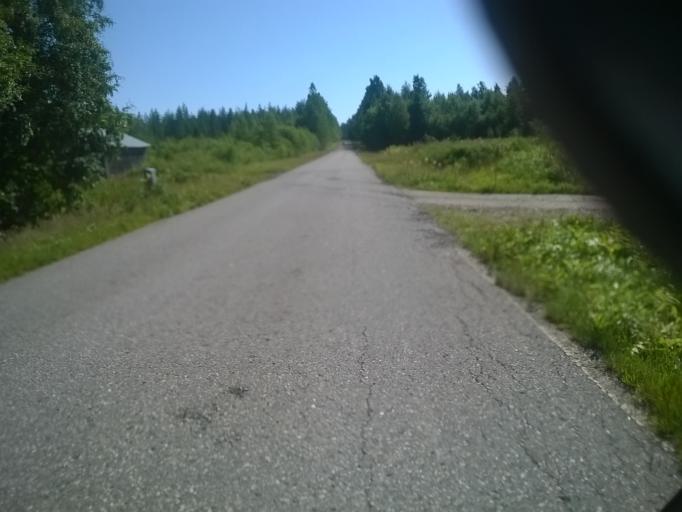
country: FI
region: Kainuu
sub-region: Kehys-Kainuu
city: Kuhmo
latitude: 64.1324
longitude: 29.4403
